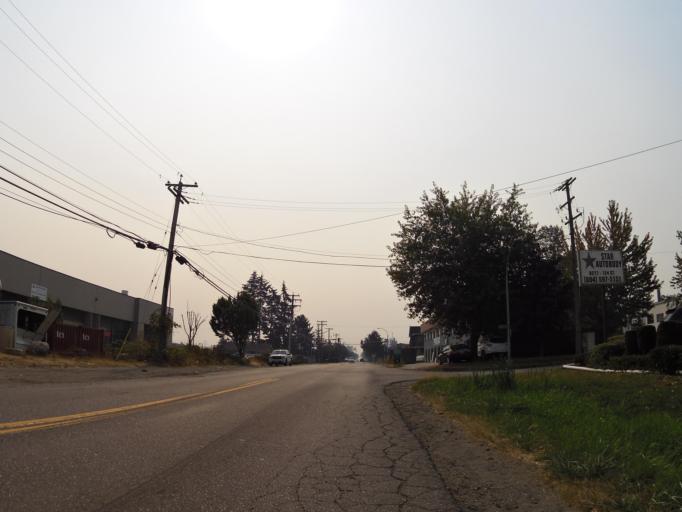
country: CA
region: British Columbia
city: Delta
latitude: 49.1534
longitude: -122.8791
